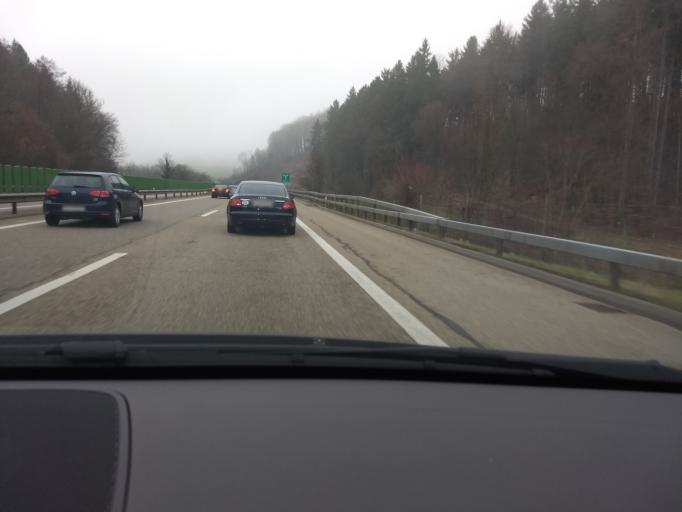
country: CH
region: Basel-Landschaft
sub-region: Bezirk Liestal
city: Arisdorf
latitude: 47.5196
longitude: 7.7537
